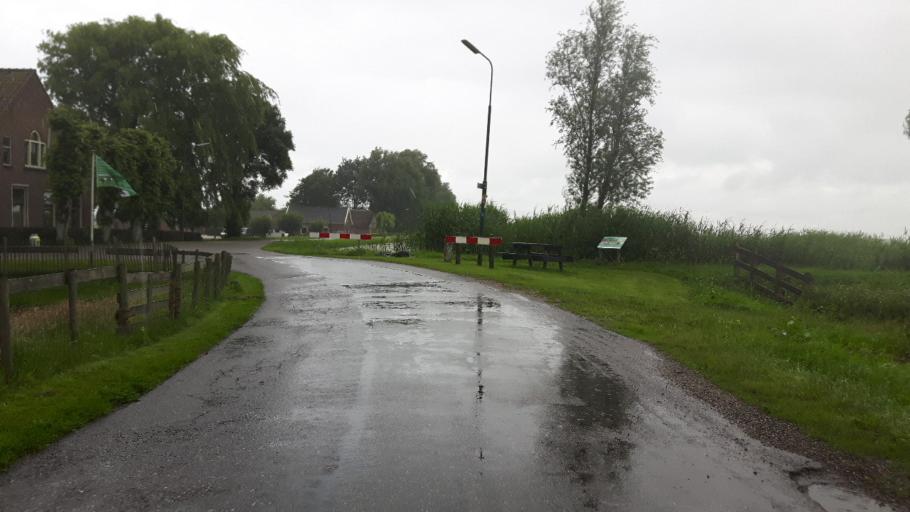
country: NL
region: Utrecht
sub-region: Stichtse Vecht
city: Spechtenkamp
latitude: 52.1338
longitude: 4.9609
